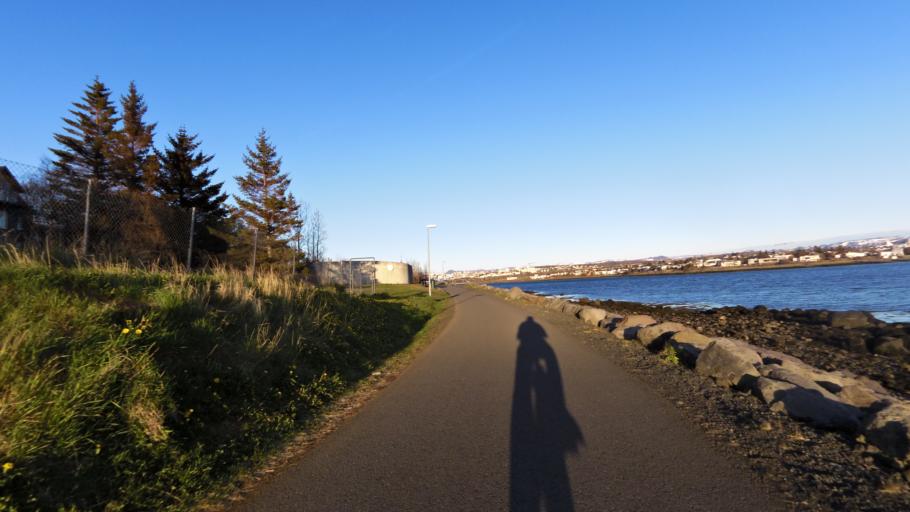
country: IS
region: Capital Region
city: Kopavogur
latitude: 64.1085
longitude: -21.9353
